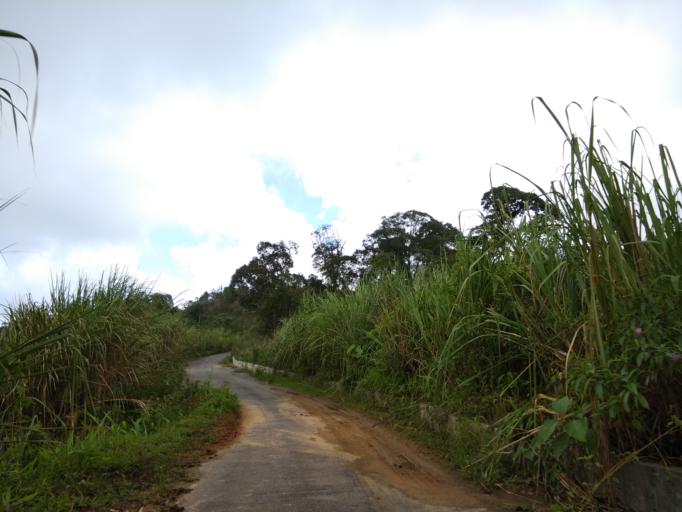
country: BD
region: Chittagong
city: Bandarban
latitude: 21.7377
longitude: 92.4203
